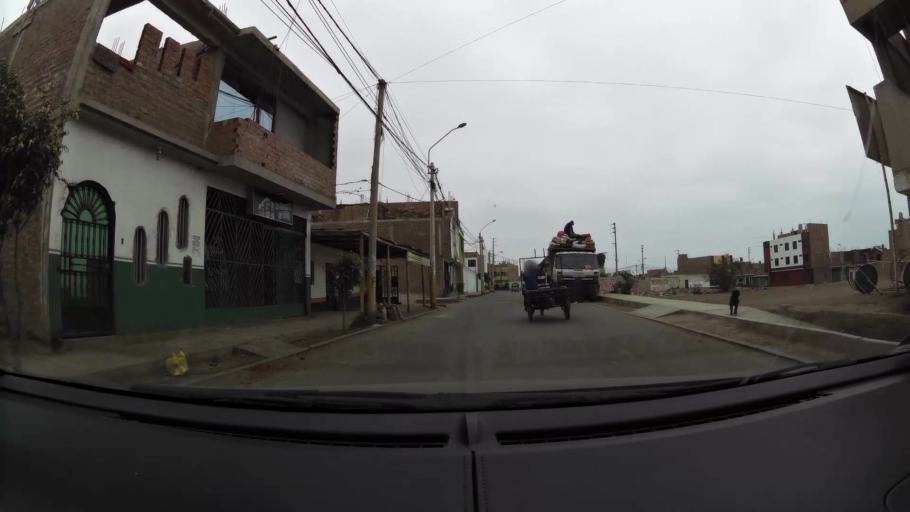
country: PE
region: Lima
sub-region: Barranca
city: Barranca
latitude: -10.7437
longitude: -77.7556
